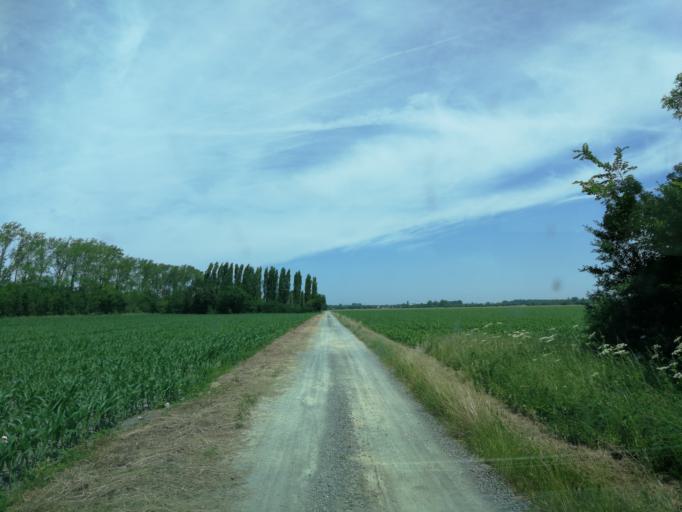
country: FR
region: Poitou-Charentes
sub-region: Departement de la Charente-Maritime
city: Marans
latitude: 46.3684
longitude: -0.9594
